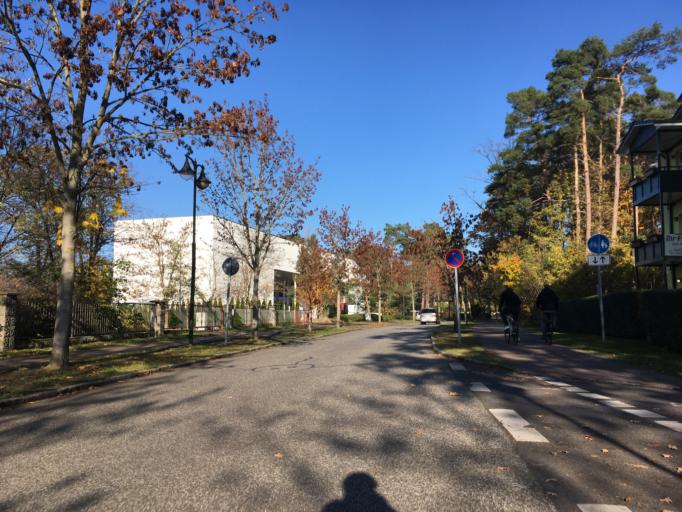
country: DE
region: Brandenburg
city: Bad Saarow
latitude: 52.2860
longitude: 14.0572
